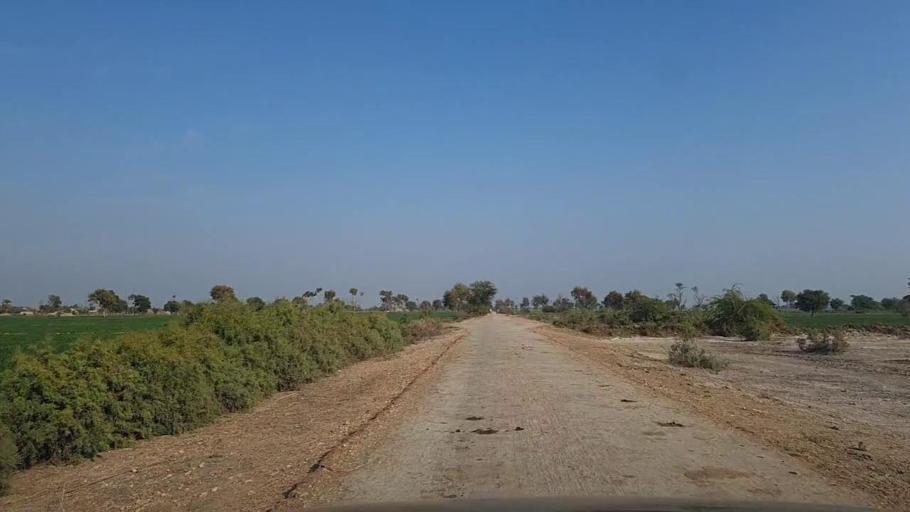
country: PK
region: Sindh
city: Nawabshah
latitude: 26.3874
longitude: 68.4538
